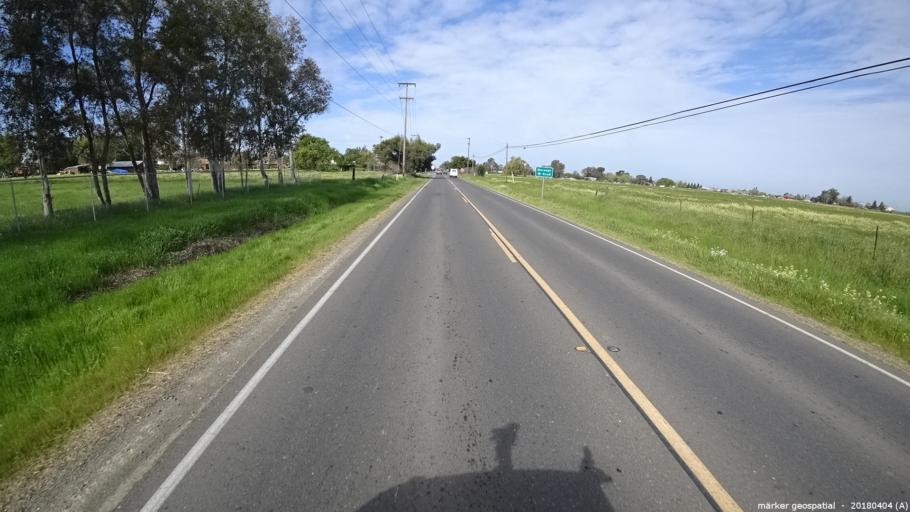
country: US
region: California
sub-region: Sacramento County
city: Herald
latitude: 38.2913
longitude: -121.2812
